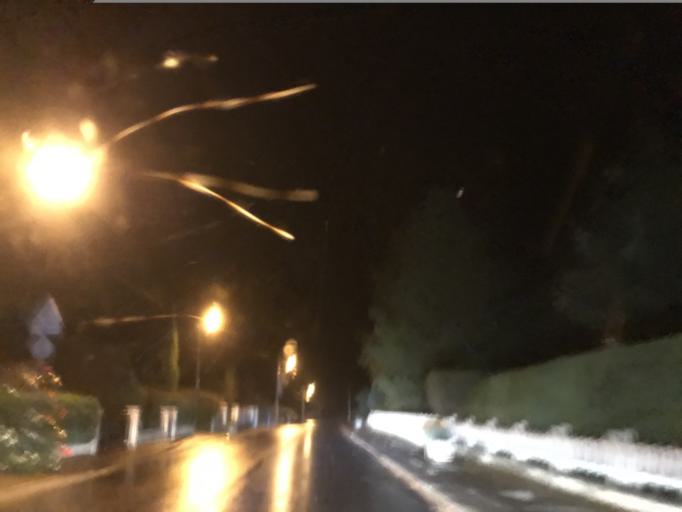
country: FR
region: Auvergne
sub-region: Departement du Puy-de-Dome
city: Celles-sur-Durolle
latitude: 45.8835
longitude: 3.6425
